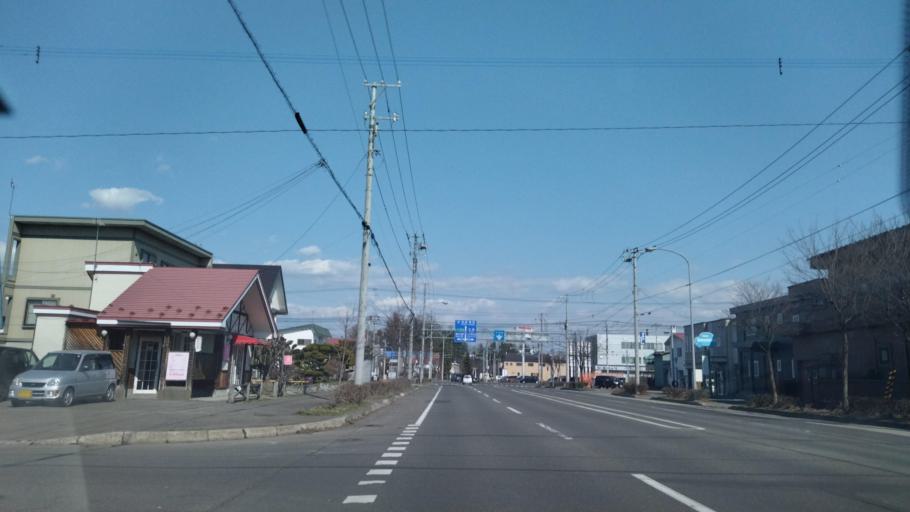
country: JP
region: Hokkaido
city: Obihiro
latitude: 42.8993
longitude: 143.2066
